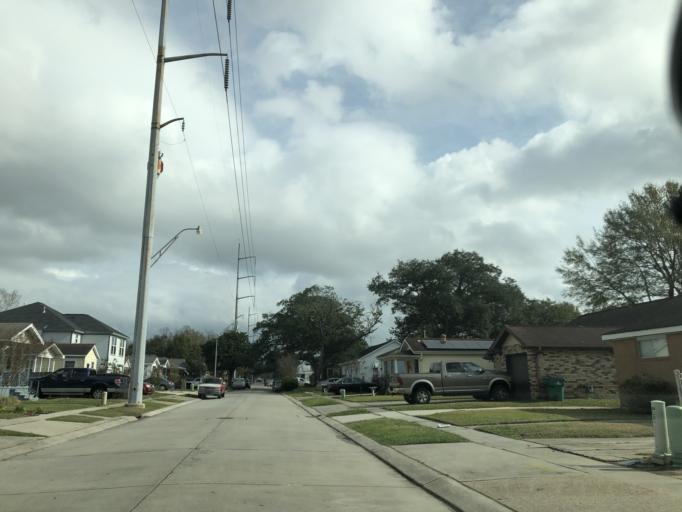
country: US
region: Louisiana
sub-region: Jefferson Parish
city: Metairie Terrace
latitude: 29.9768
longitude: -90.1664
